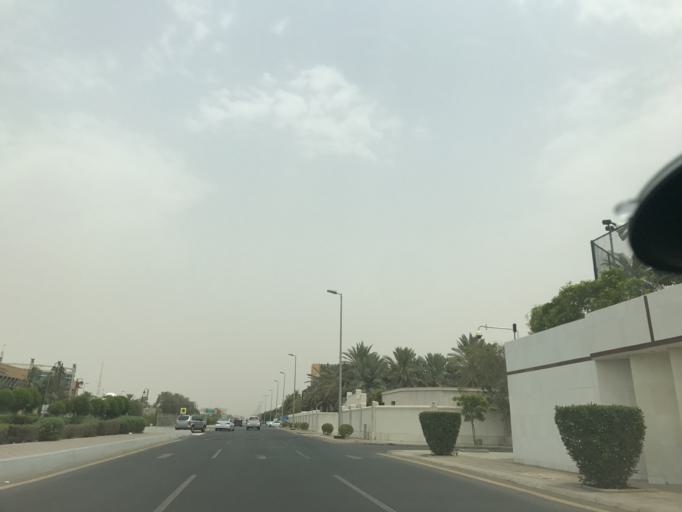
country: SA
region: Makkah
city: Jeddah
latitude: 21.5524
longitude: 39.1531
